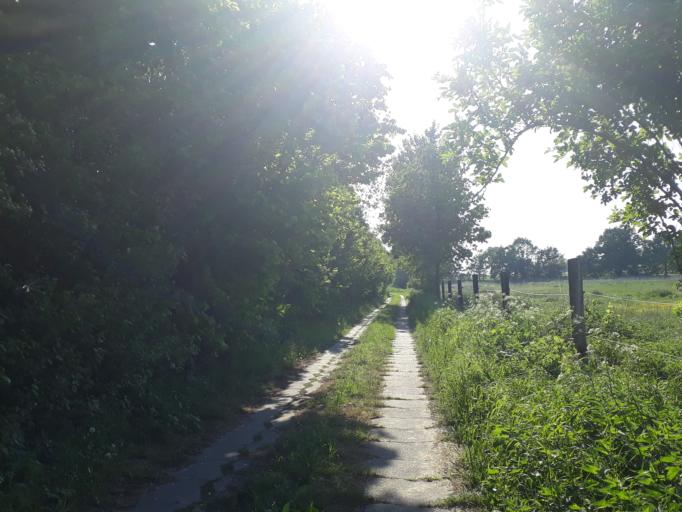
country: DE
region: Brandenburg
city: Potsdam
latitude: 52.4565
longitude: 13.0051
